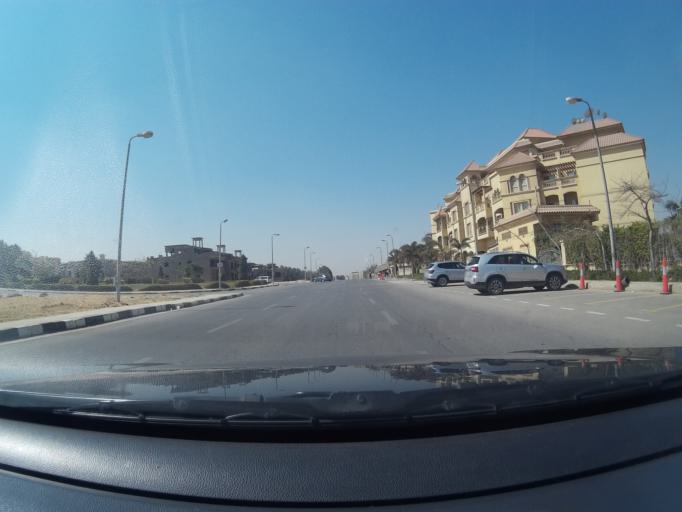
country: EG
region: Muhafazat al Qahirah
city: Cairo
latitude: 30.0136
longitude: 31.4086
